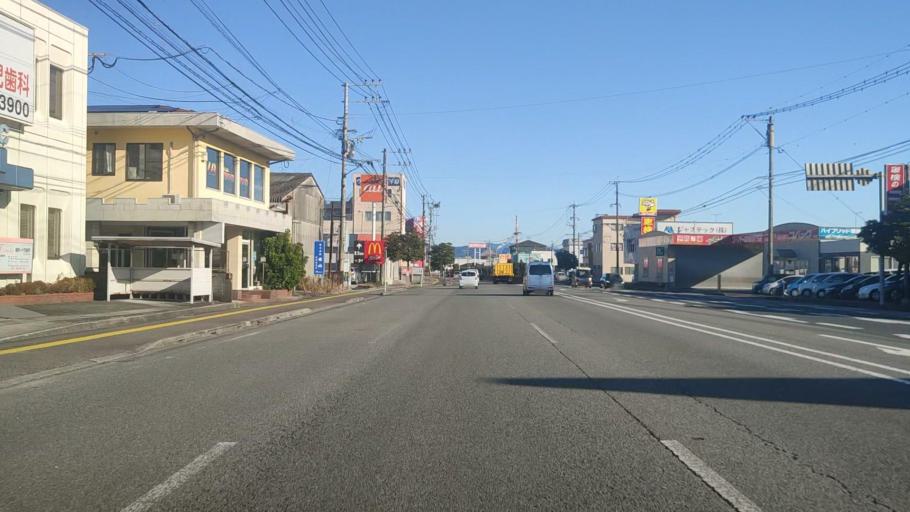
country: JP
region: Miyazaki
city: Nobeoka
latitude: 32.5523
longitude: 131.6782
